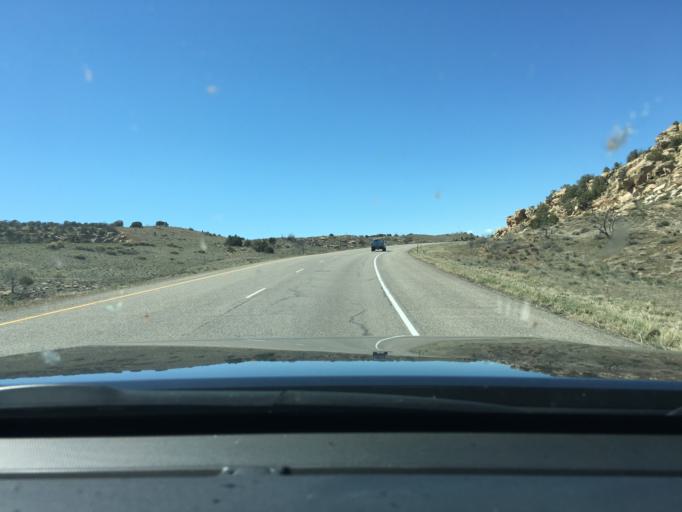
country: US
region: Colorado
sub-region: Mesa County
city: Loma
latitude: 39.1883
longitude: -109.0342
